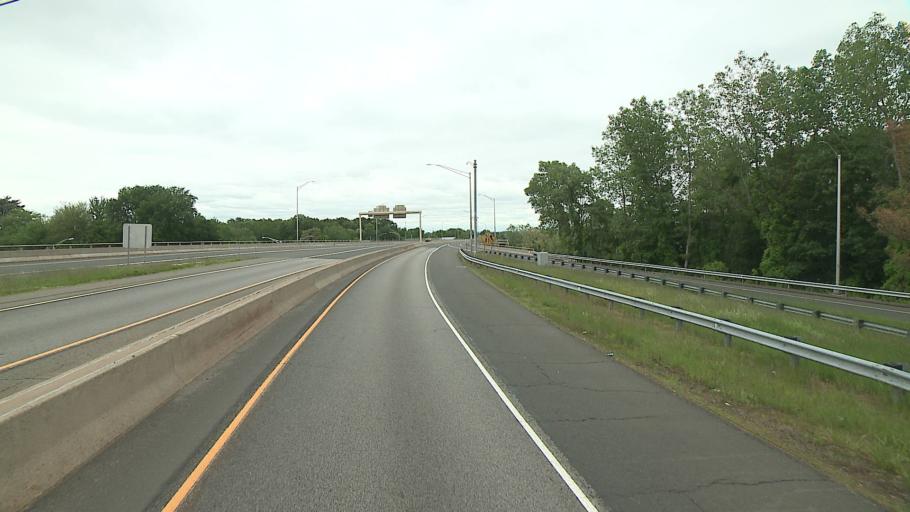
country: US
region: Connecticut
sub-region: Hartford County
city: Blue Hills
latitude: 41.8184
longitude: -72.6678
